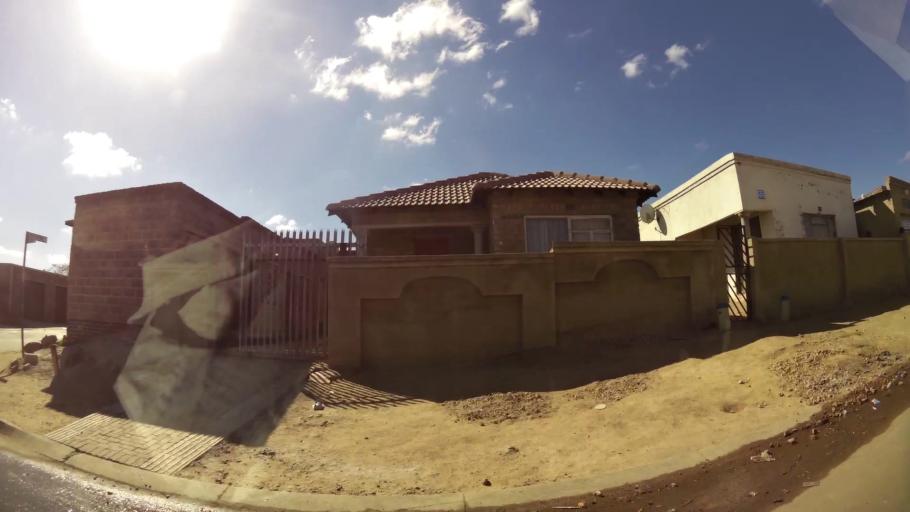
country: ZA
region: Gauteng
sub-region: City of Johannesburg Metropolitan Municipality
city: Midrand
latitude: -26.0323
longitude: 28.1609
